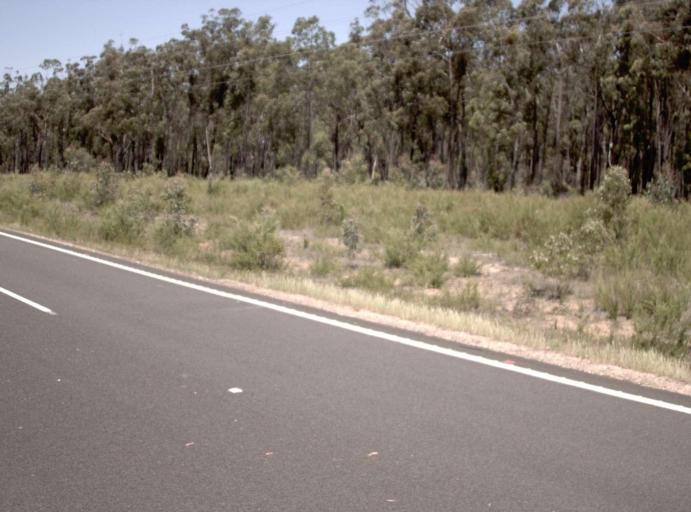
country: AU
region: Victoria
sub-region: East Gippsland
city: Lakes Entrance
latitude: -37.7370
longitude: 148.1497
